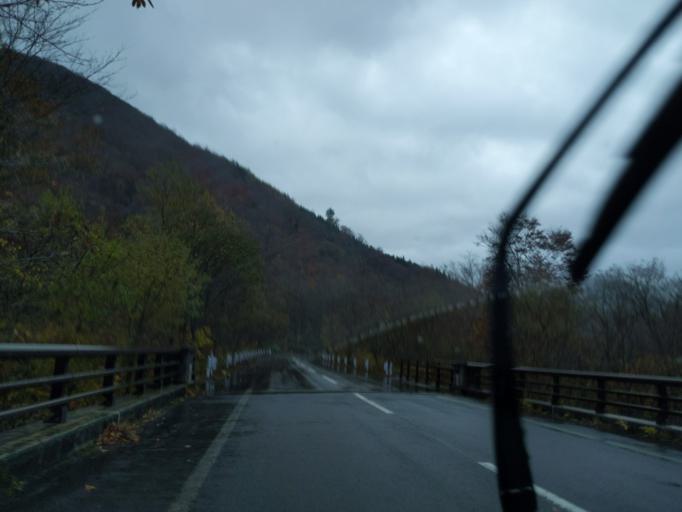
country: JP
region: Iwate
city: Mizusawa
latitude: 39.0529
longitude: 140.8544
